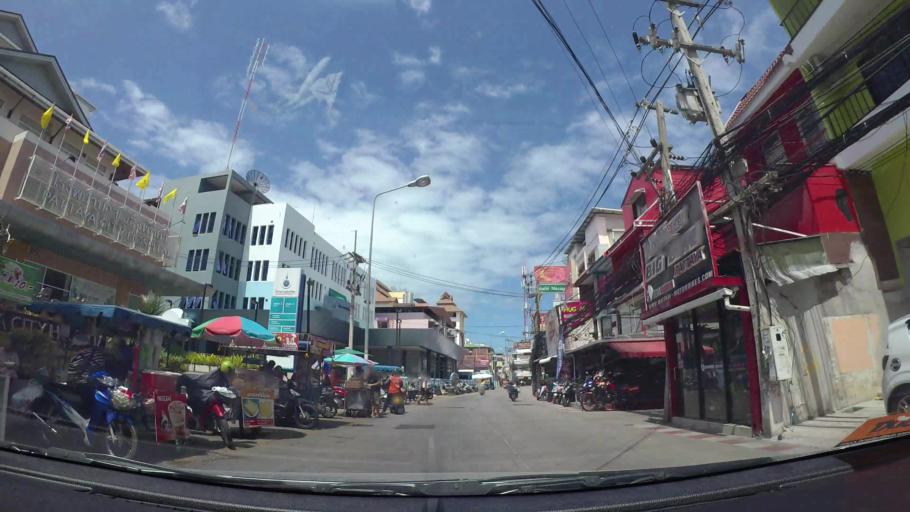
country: TH
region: Chon Buri
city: Phatthaya
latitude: 12.9281
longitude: 100.8843
